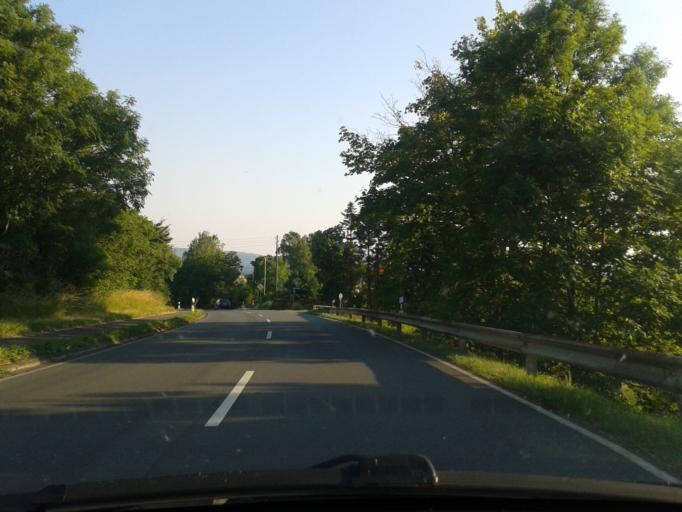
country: DE
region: North Rhine-Westphalia
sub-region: Regierungsbezirk Detmold
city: Detmold
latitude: 51.9592
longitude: 8.9089
